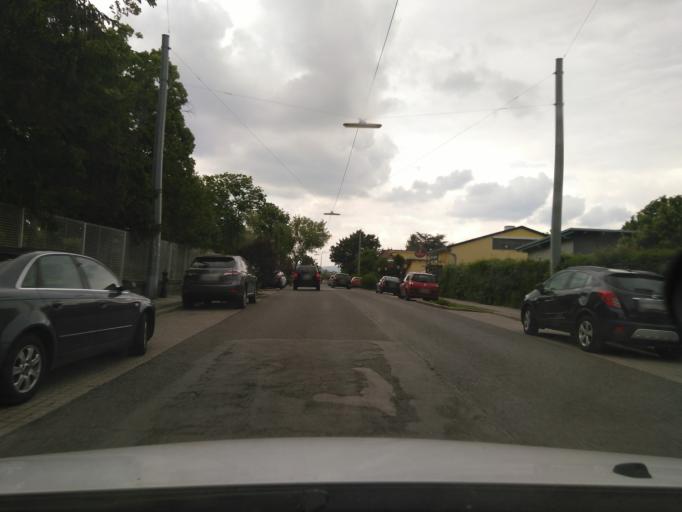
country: AT
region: Lower Austria
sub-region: Politischer Bezirk Modling
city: Perchtoldsdorf
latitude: 48.1604
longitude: 16.2913
